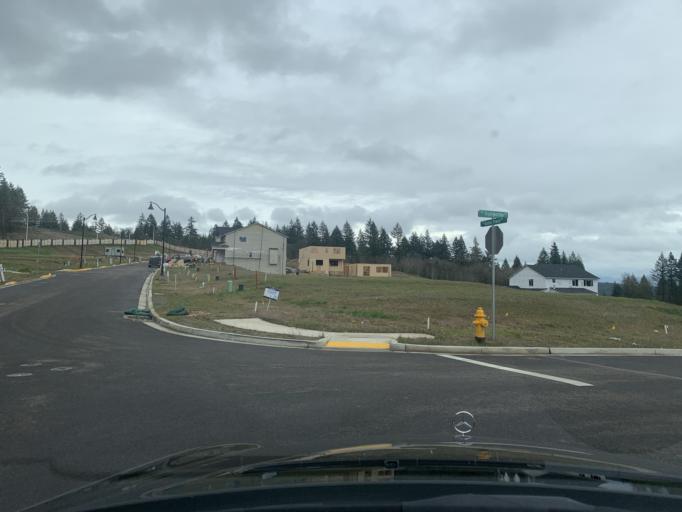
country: US
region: Oregon
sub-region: Clackamas County
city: Happy Valley
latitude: 45.4420
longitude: -122.5084
